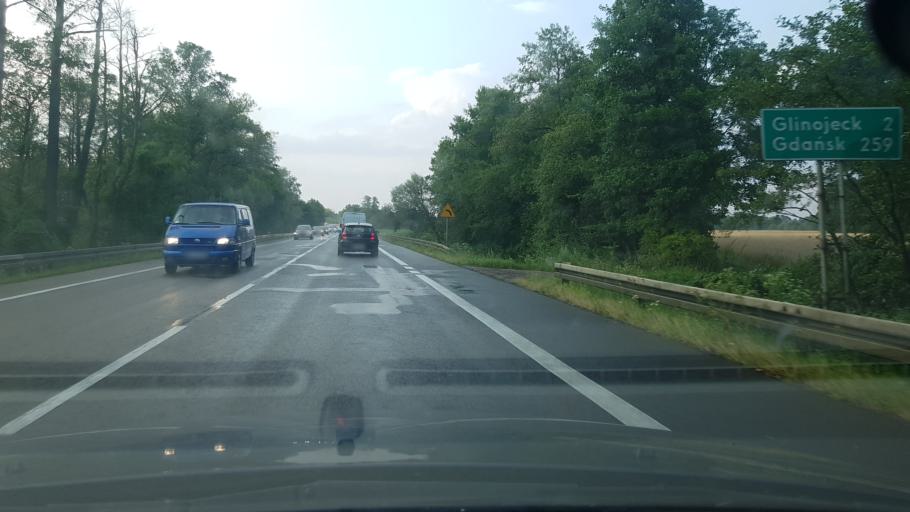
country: PL
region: Masovian Voivodeship
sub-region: Powiat ciechanowski
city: Glinojeck
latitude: 52.8039
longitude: 20.2700
